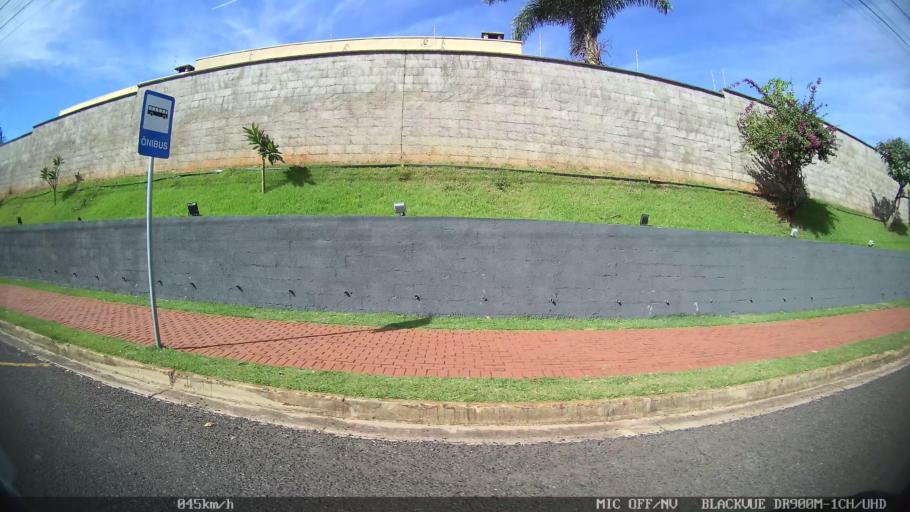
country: BR
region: Sao Paulo
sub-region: Sao Jose Do Rio Preto
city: Sao Jose do Rio Preto
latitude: -20.8023
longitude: -49.3324
